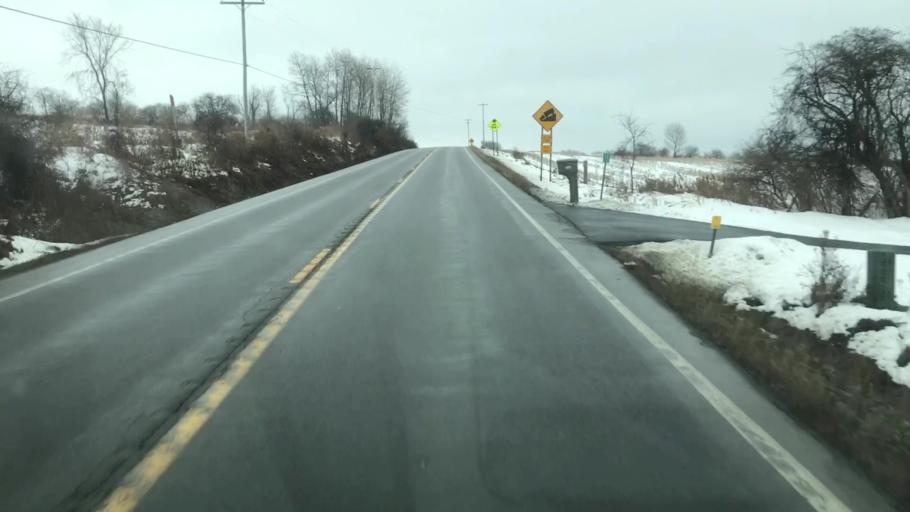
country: US
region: New York
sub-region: Cortland County
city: Cortland West
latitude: 42.6405
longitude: -76.2264
